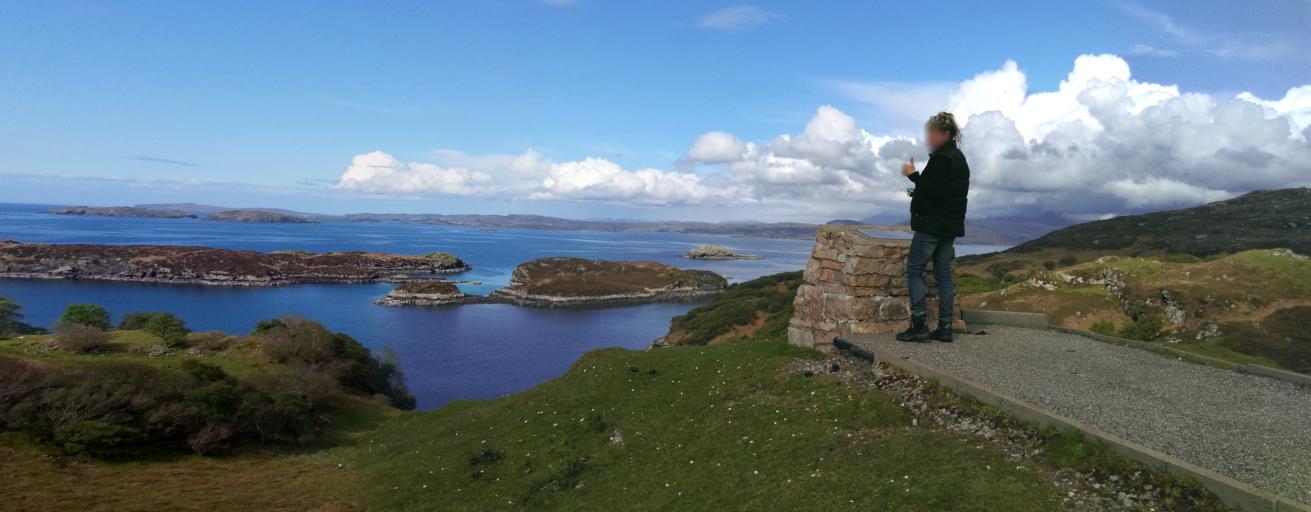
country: GB
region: Scotland
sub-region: Highland
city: Ullapool
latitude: 58.2446
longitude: -5.2050
